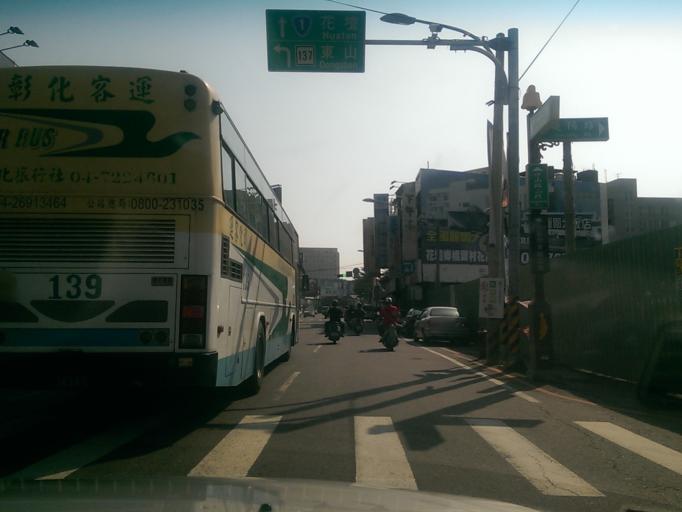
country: TW
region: Taiwan
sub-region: Changhua
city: Chang-hua
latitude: 24.0720
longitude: 120.5428
